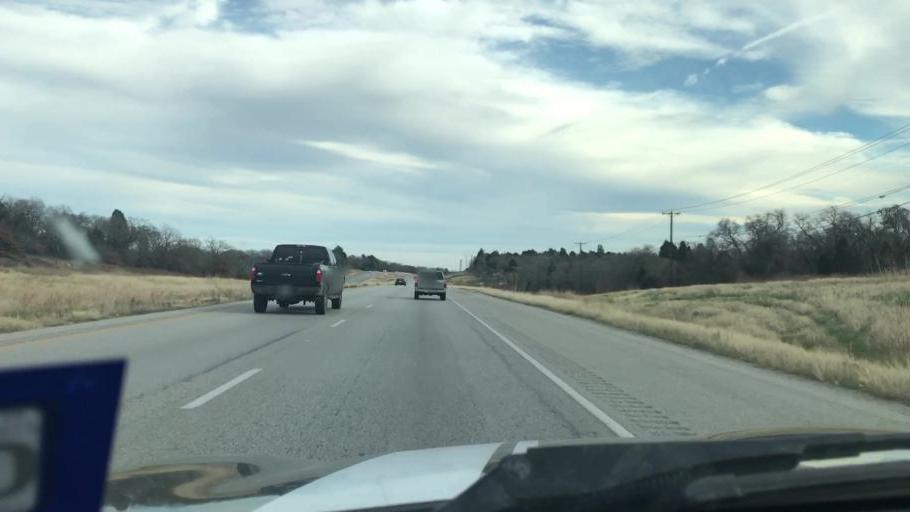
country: US
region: Texas
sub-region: Bastrop County
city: Elgin
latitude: 30.3273
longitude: -97.3356
